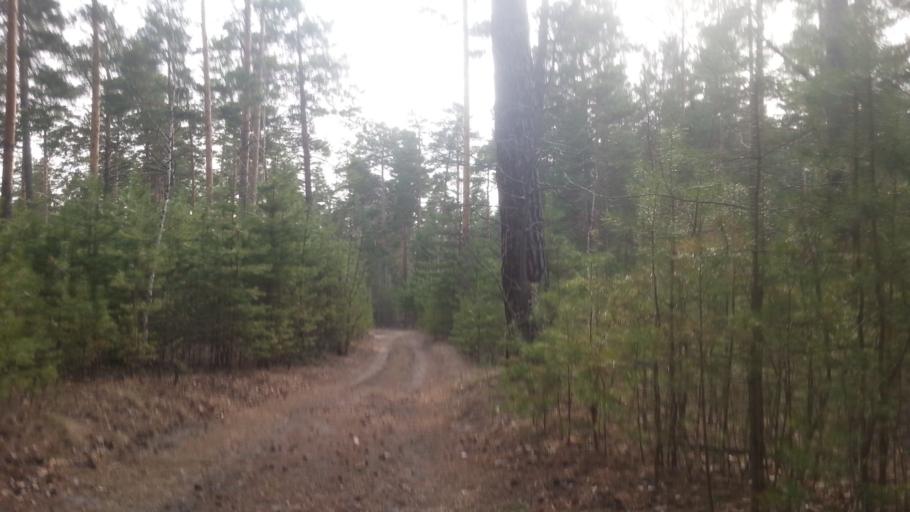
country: RU
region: Altai Krai
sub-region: Gorod Barnaulskiy
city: Barnaul
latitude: 53.3244
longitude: 83.7189
